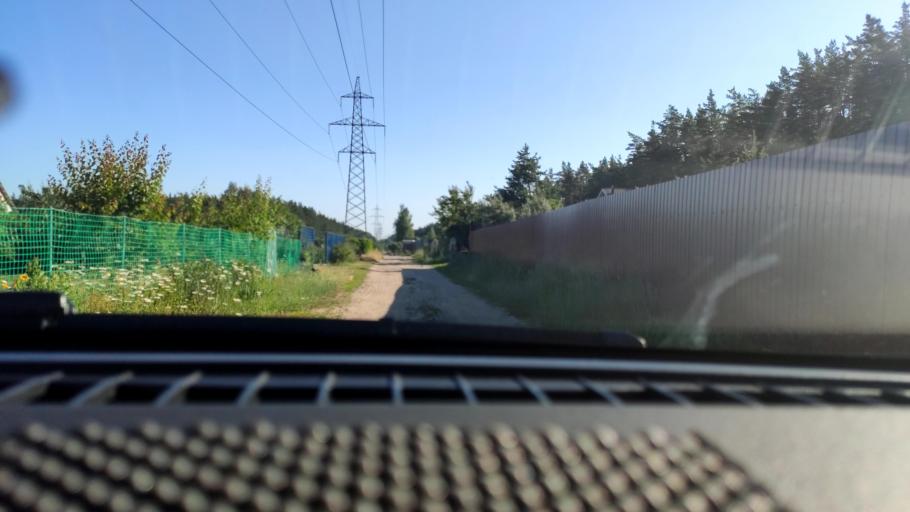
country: RU
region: Voronezj
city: Volya
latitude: 51.7424
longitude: 39.4603
